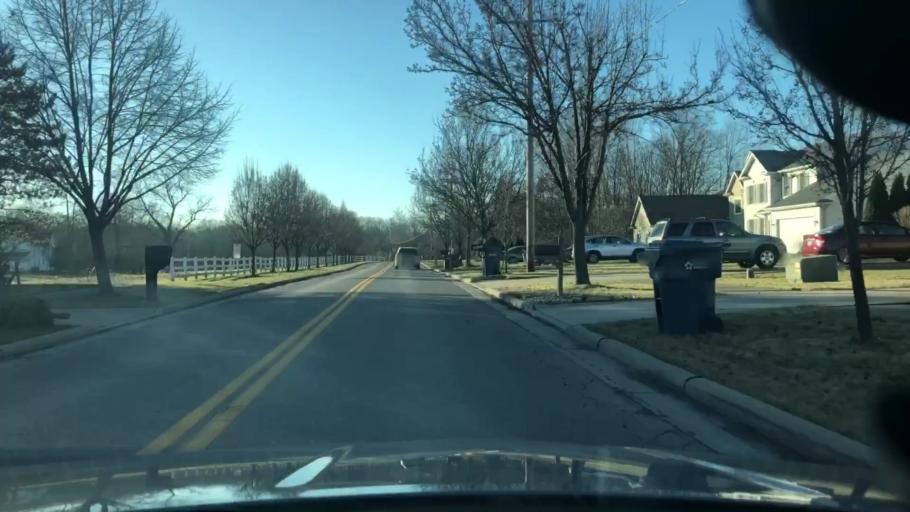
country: US
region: Ohio
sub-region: Cuyahoga County
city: Olmsted Falls
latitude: 41.3656
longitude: -81.8927
